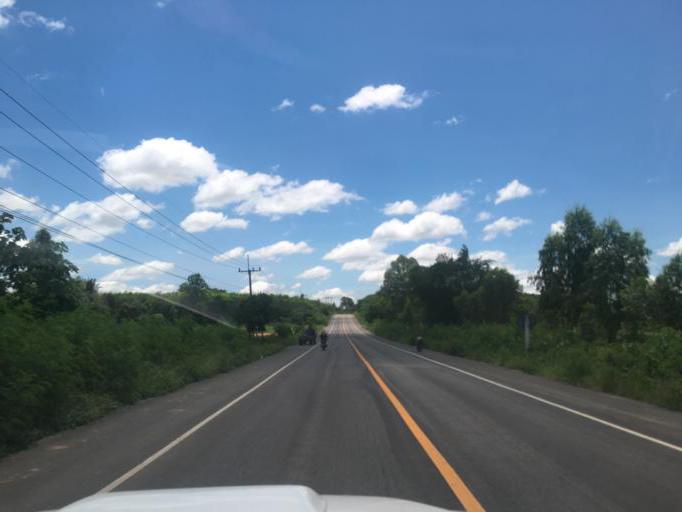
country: TH
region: Changwat Udon Thani
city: Nong Saeng
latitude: 17.2269
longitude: 102.7231
